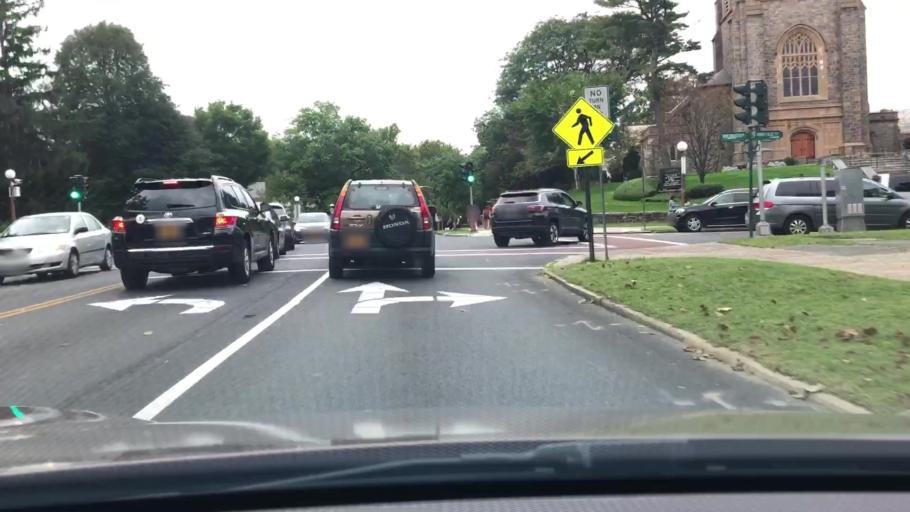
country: US
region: New York
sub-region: Westchester County
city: Bronxville
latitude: 40.9366
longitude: -73.8311
